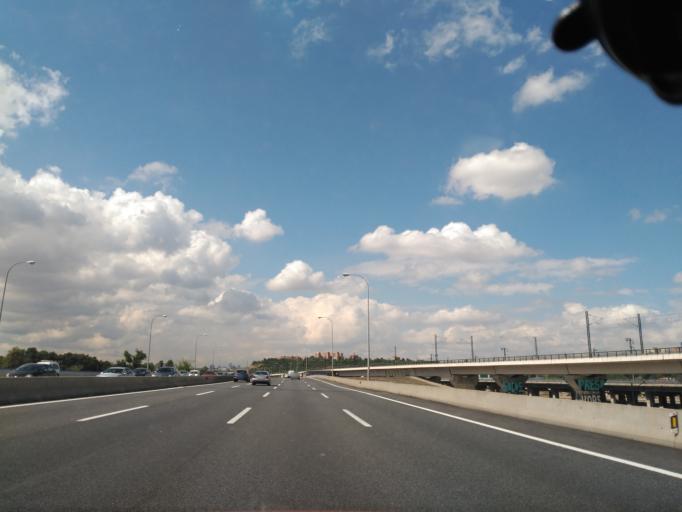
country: ES
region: Madrid
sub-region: Provincia de Madrid
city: Villaverde
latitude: 40.3653
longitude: -3.6782
